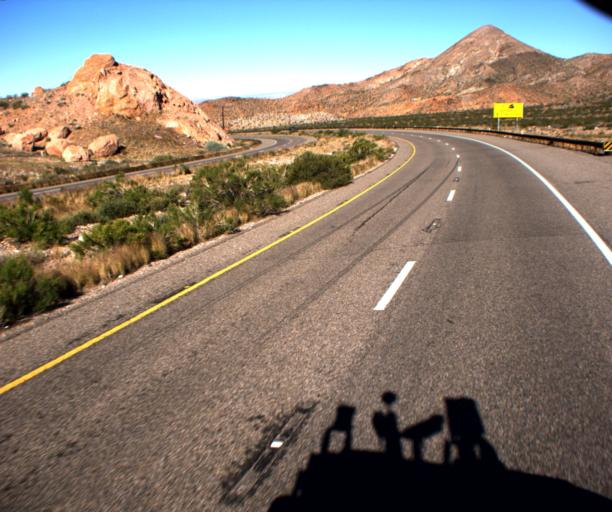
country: US
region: Nevada
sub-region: Clark County
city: Laughlin
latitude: 35.1997
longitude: -114.4215
